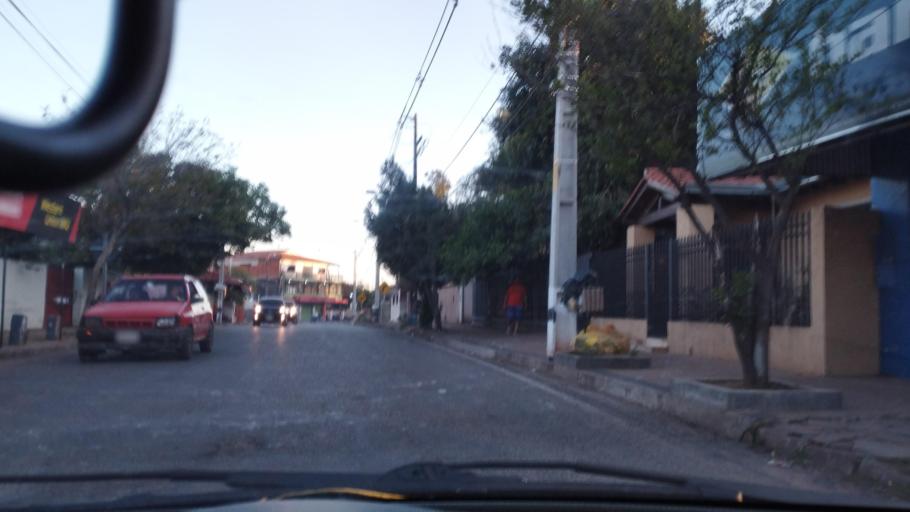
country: PY
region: Central
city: Fernando de la Mora
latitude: -25.3019
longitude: -57.5303
